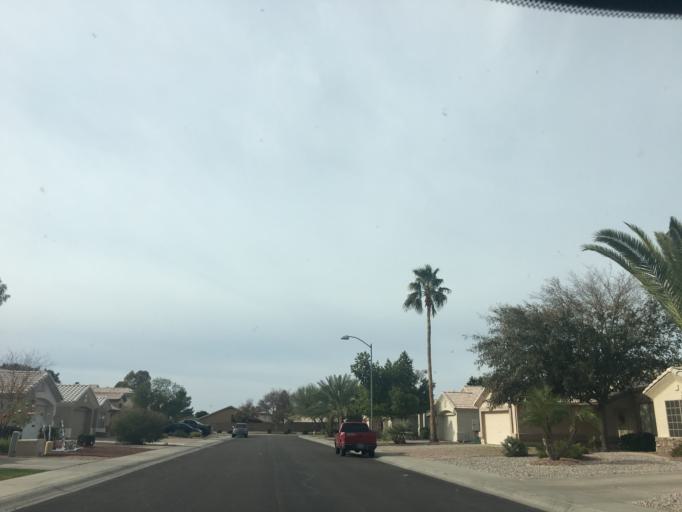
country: US
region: Arizona
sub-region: Maricopa County
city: Gilbert
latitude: 33.3467
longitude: -111.7990
